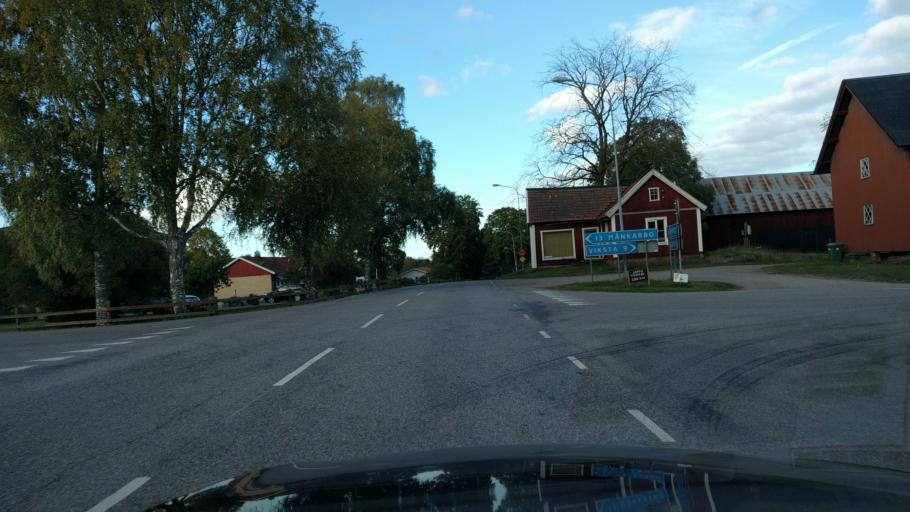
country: SE
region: Uppsala
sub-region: Osthammars Kommun
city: Bjorklinge
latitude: 60.1442
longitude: 17.5761
